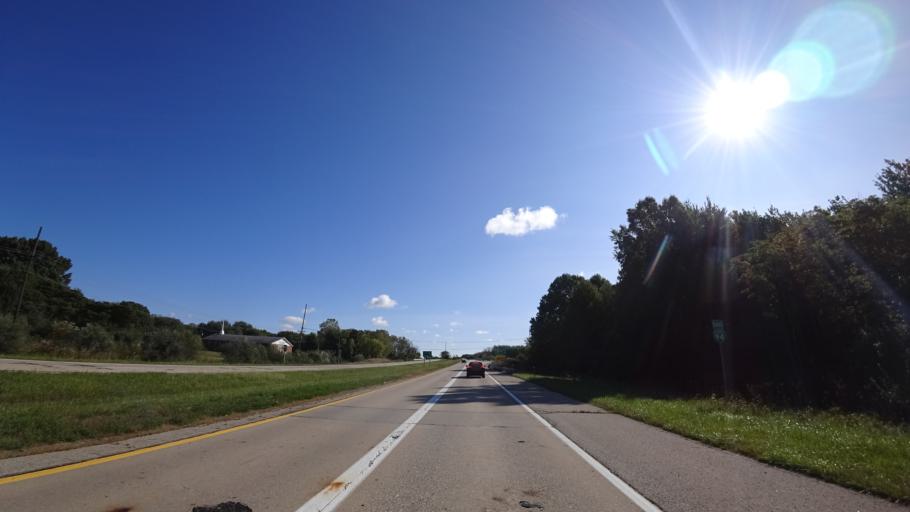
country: US
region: Michigan
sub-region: Berrien County
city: Benton Heights
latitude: 42.1191
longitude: -86.3963
